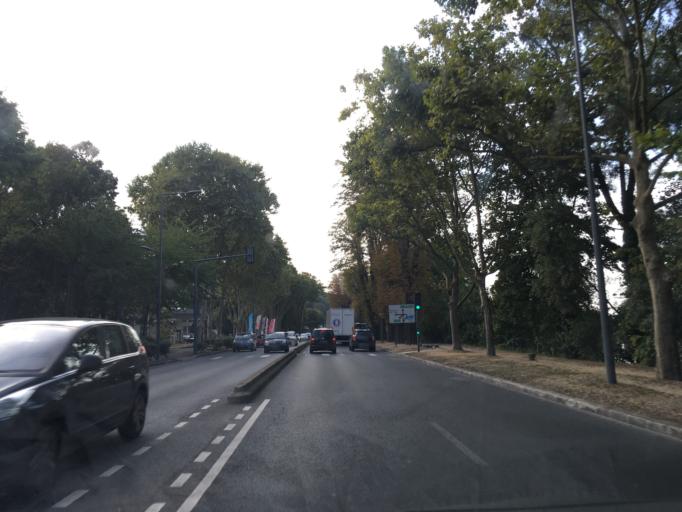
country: FR
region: Ile-de-France
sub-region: Departement des Yvelines
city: Bougival
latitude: 48.8683
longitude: 2.1328
